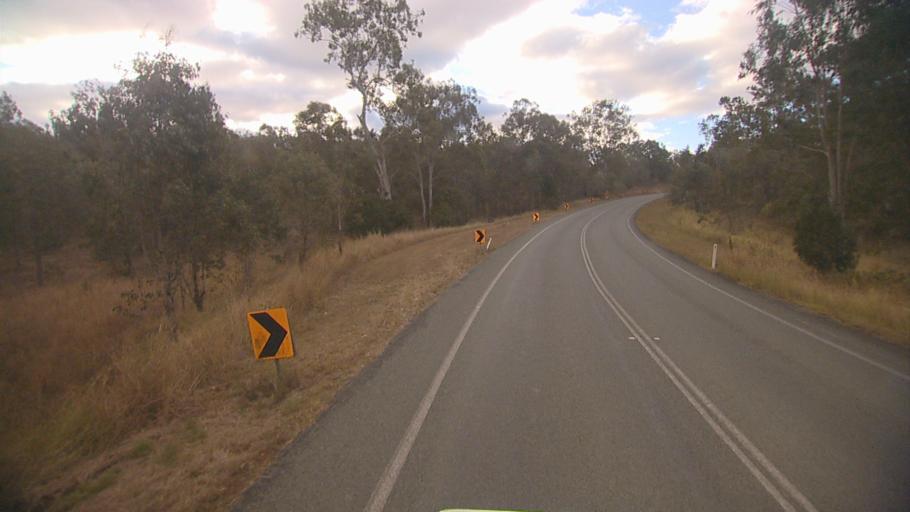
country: AU
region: Queensland
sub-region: Logan
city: Cedar Vale
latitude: -27.9091
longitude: 153.0899
